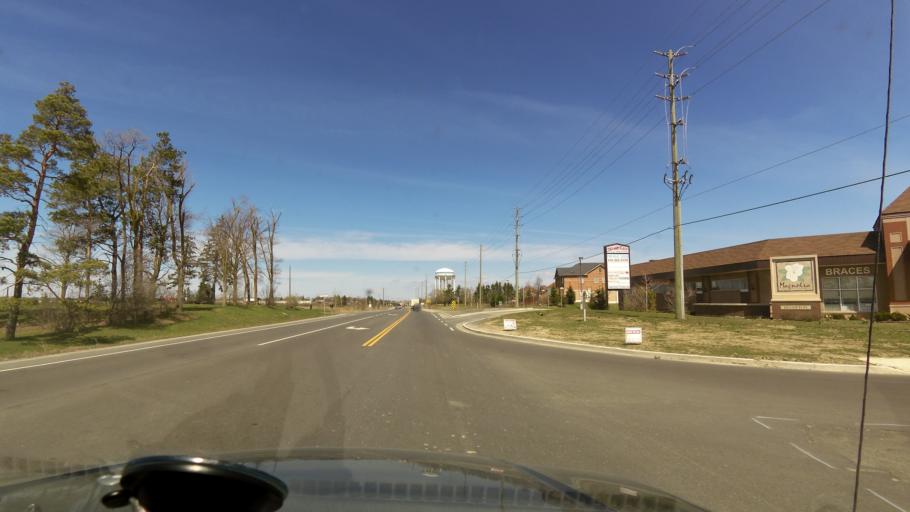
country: CA
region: Ontario
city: Brampton
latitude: 43.7261
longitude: -79.8329
